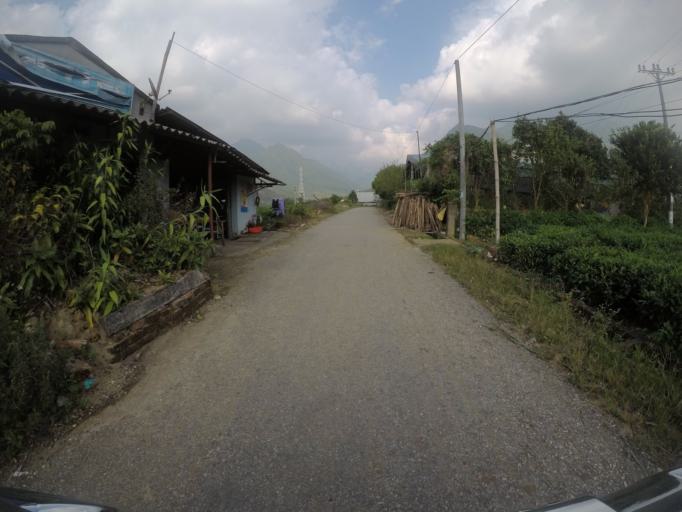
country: VN
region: Lai Chau
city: Tam Duong
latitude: 22.2168
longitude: 103.7456
